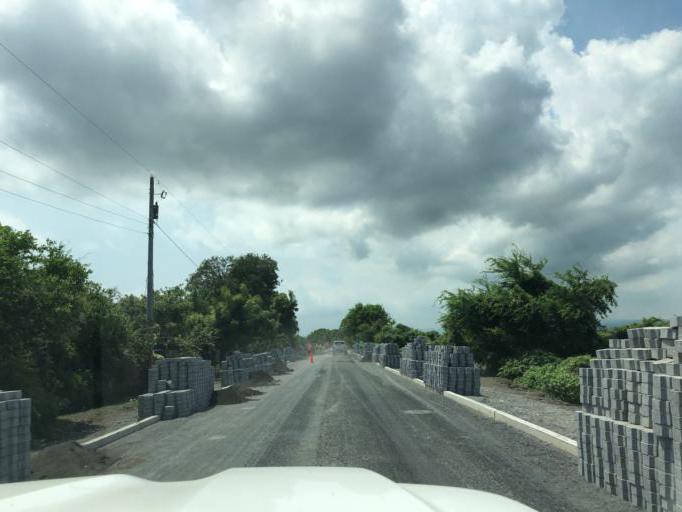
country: NI
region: Masaya
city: Tisma
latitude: 12.0397
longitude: -85.9215
